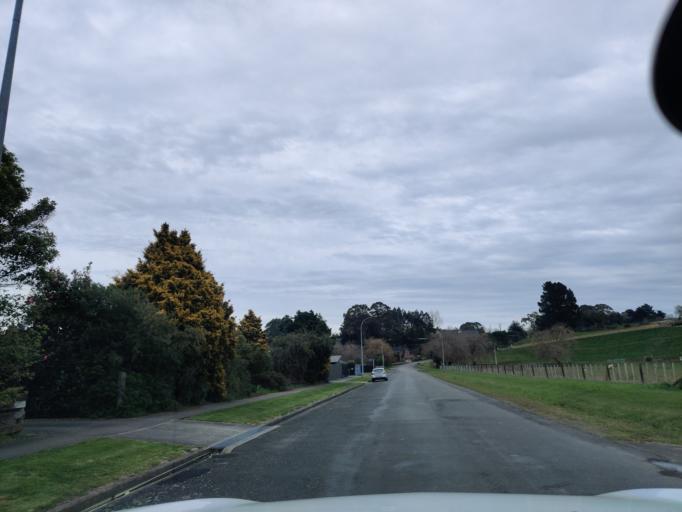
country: NZ
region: Manawatu-Wanganui
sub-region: Palmerston North City
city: Palmerston North
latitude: -40.2843
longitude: 175.7501
